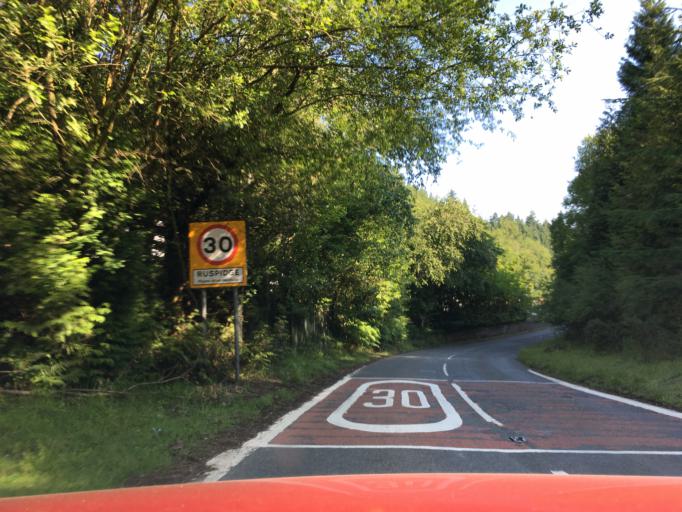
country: GB
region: England
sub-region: Gloucestershire
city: Cinderford
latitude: 51.7991
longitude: -2.5100
